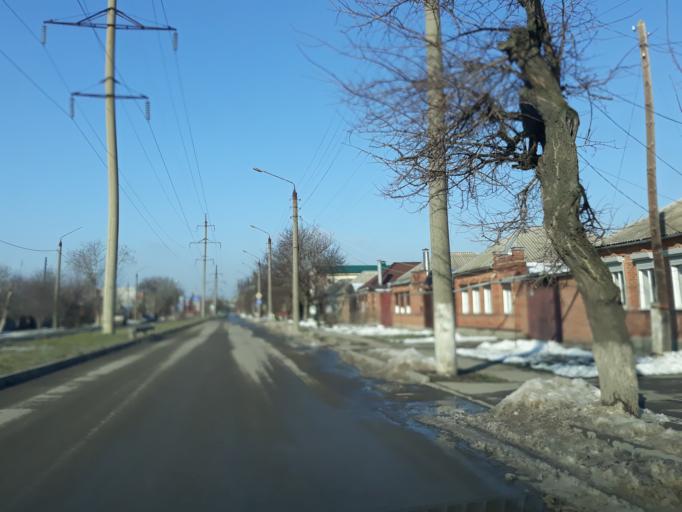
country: RU
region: Rostov
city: Taganrog
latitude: 47.2193
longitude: 38.8802
